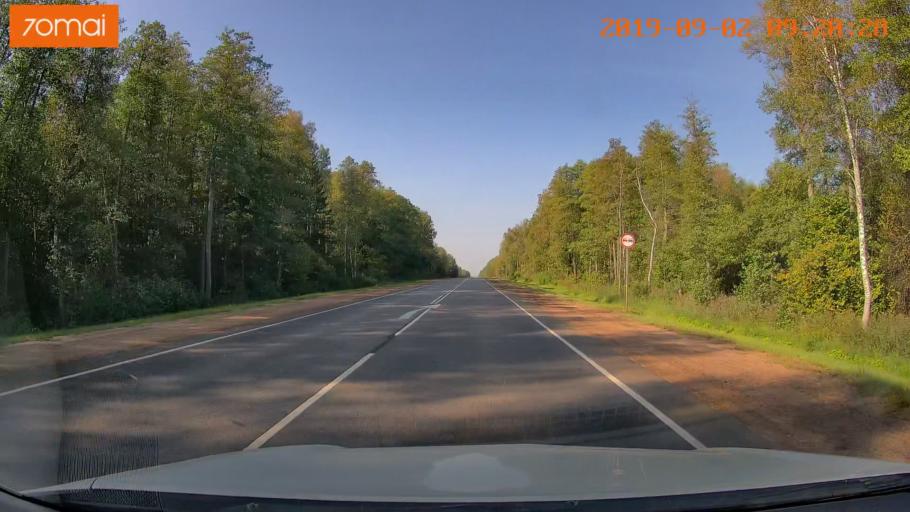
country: RU
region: Kaluga
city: Yukhnov
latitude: 54.8001
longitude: 35.3828
